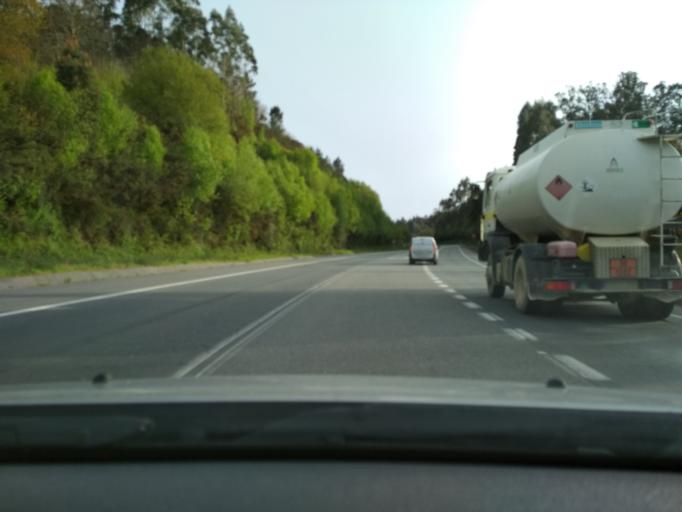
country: ES
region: Galicia
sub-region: Provincia da Coruna
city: Cerceda
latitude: 43.2150
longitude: -8.4561
